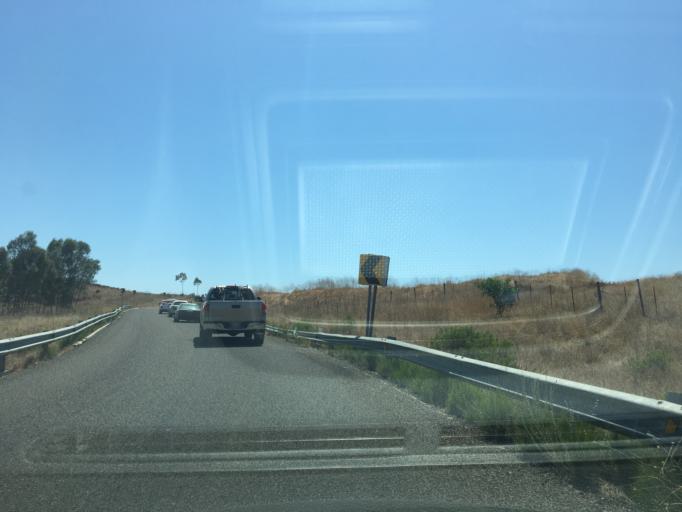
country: MX
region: Baja California
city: El Sauzal
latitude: 31.9929
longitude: -116.6982
